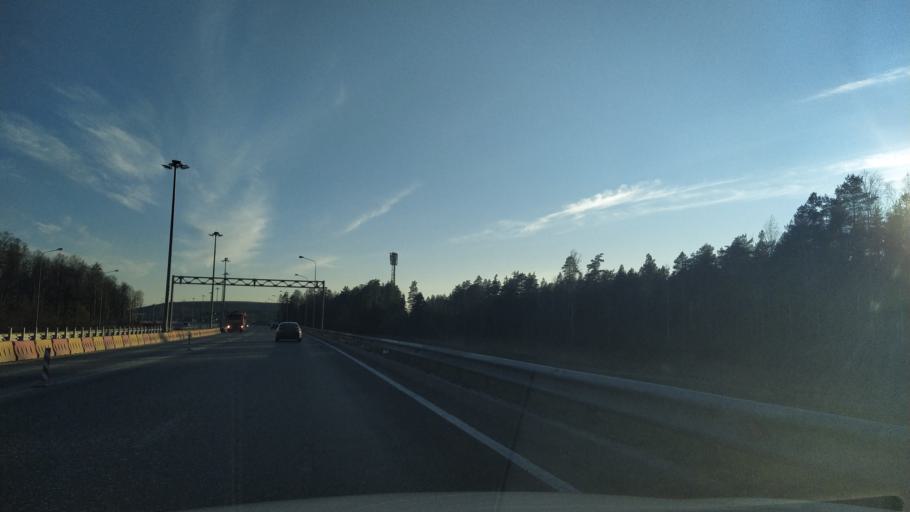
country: RU
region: St.-Petersburg
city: Levashovo
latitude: 60.0810
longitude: 30.1933
